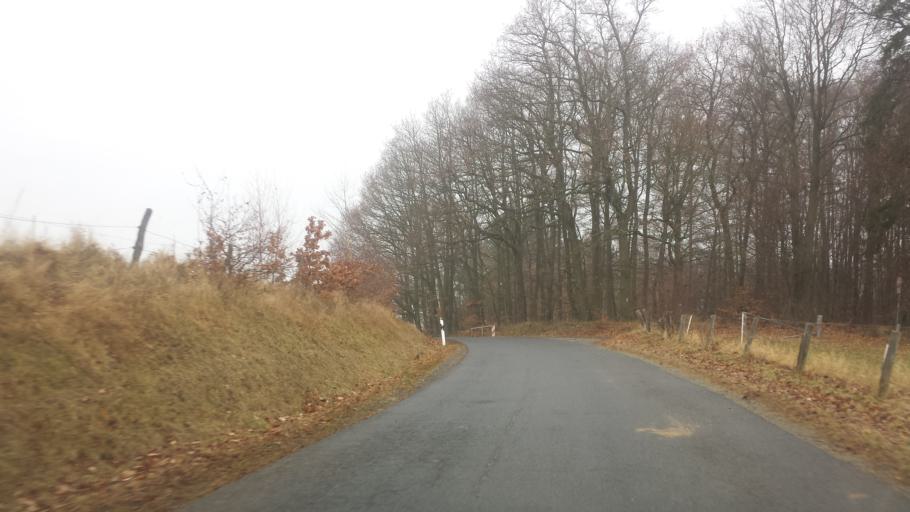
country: DE
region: Hesse
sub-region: Regierungsbezirk Darmstadt
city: Seeheim-Jugenheim
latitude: 49.7557
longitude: 8.6879
